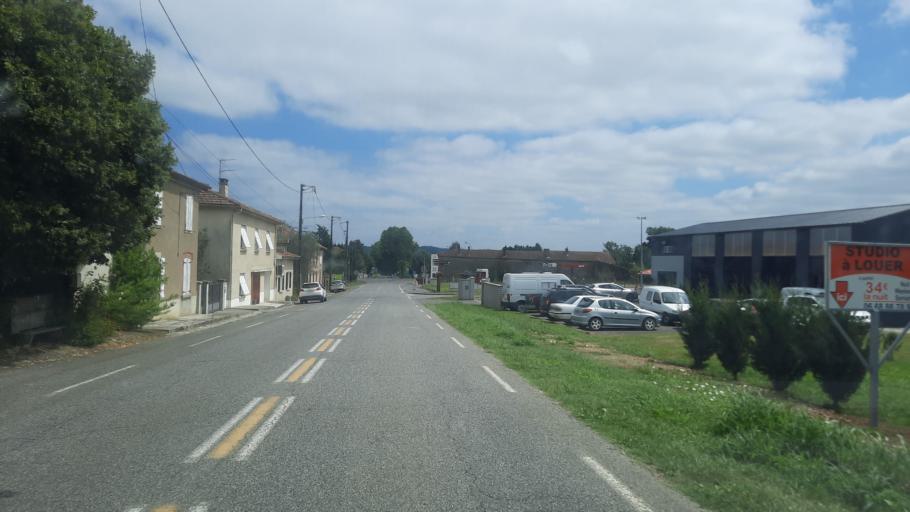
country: FR
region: Midi-Pyrenees
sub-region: Departement de la Haute-Garonne
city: Boulogne-sur-Gesse
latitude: 43.2943
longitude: 0.5142
